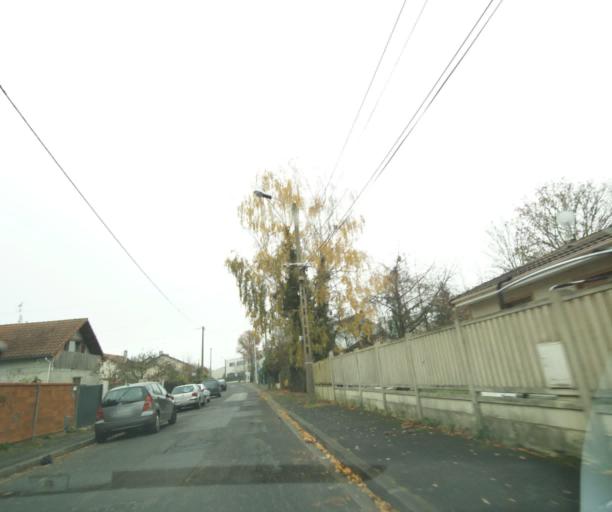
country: FR
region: Ile-de-France
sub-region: Departement de Seine-Saint-Denis
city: Vaujours
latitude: 48.9328
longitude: 2.5559
